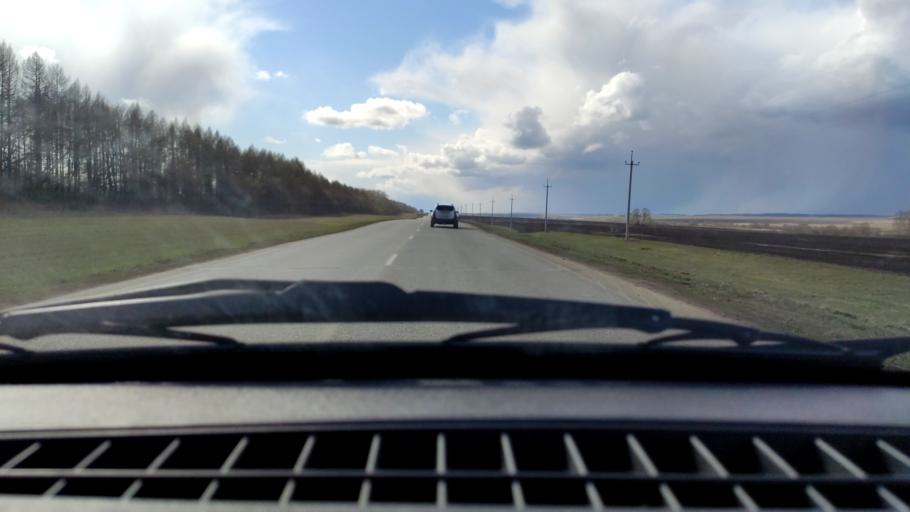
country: RU
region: Bashkortostan
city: Chekmagush
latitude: 55.1117
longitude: 54.9108
